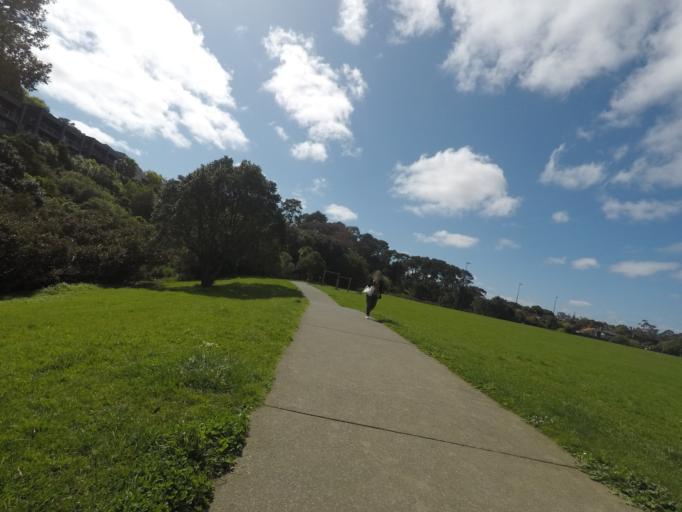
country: NZ
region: Auckland
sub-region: Auckland
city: Auckland
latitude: -36.8510
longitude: 174.7272
